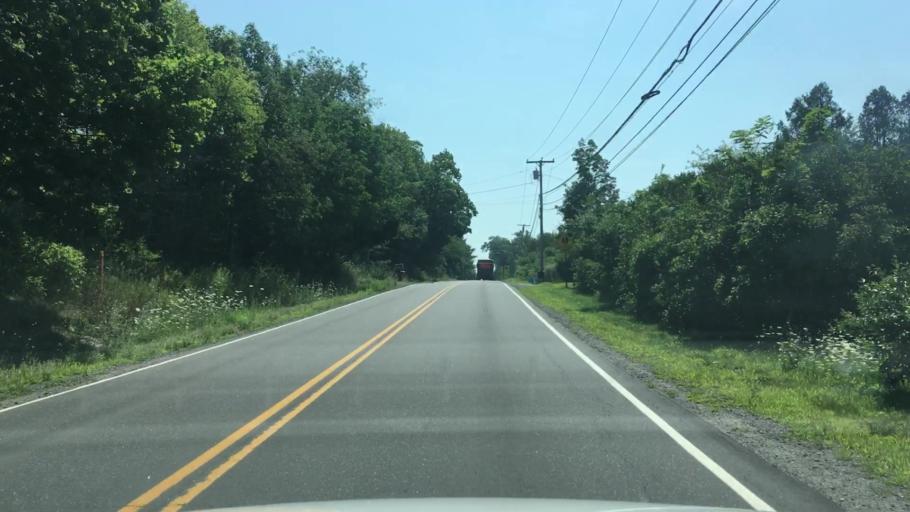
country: US
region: Maine
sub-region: Kennebec County
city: Hallowell
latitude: 44.2951
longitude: -69.8031
